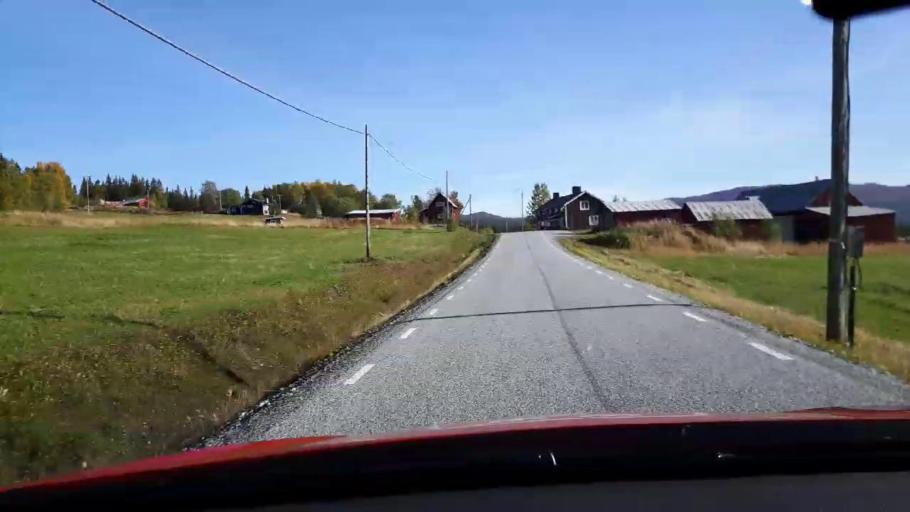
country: NO
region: Nord-Trondelag
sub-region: Royrvik
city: Royrvik
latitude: 64.8123
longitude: 14.1617
